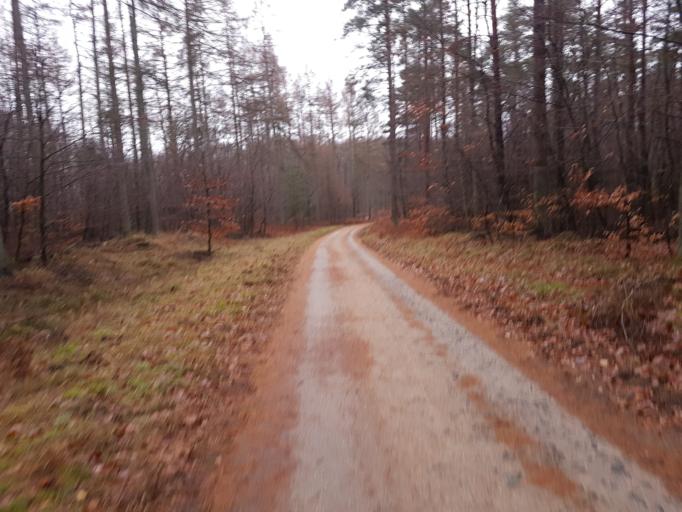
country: DE
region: Mecklenburg-Vorpommern
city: Ostseebad Sellin
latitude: 54.3924
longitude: 13.6572
